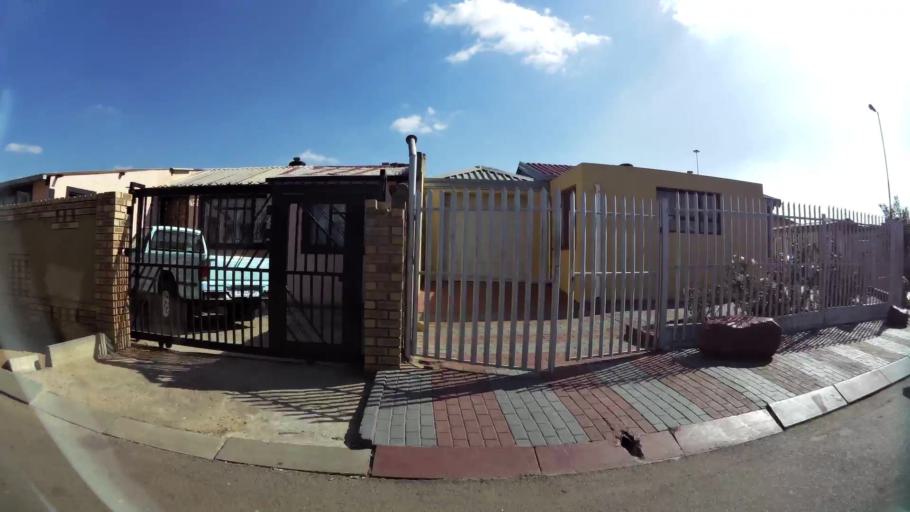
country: ZA
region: Gauteng
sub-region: City of Johannesburg Metropolitan Municipality
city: Soweto
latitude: -26.2562
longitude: 27.8889
